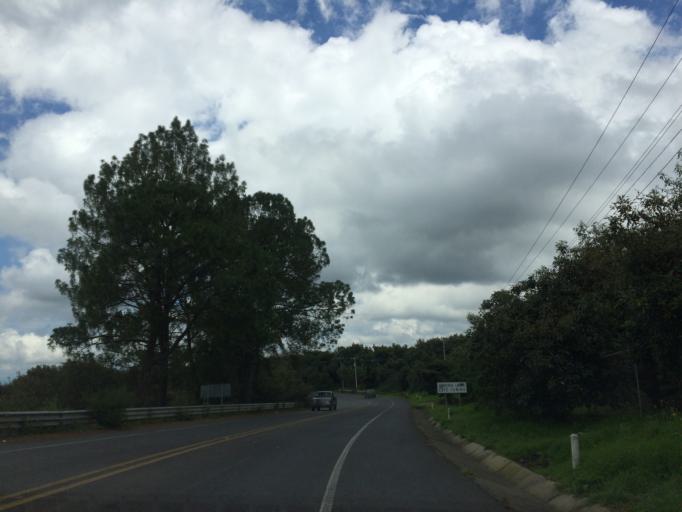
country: MX
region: Michoacan
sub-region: Uruapan
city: Nuevo Zirosto
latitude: 19.5475
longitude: -102.3356
